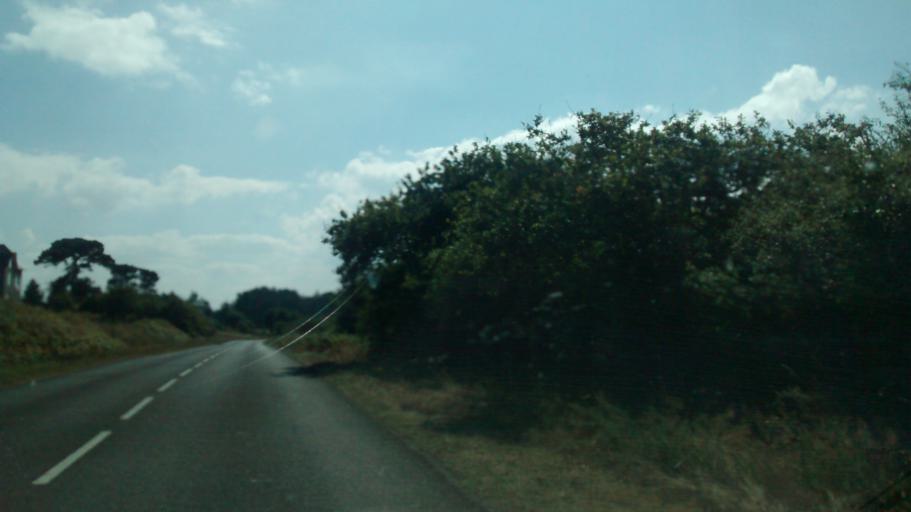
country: FR
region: Brittany
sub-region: Departement d'Ille-et-Vilaine
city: Cancale
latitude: 48.6978
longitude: -1.8604
